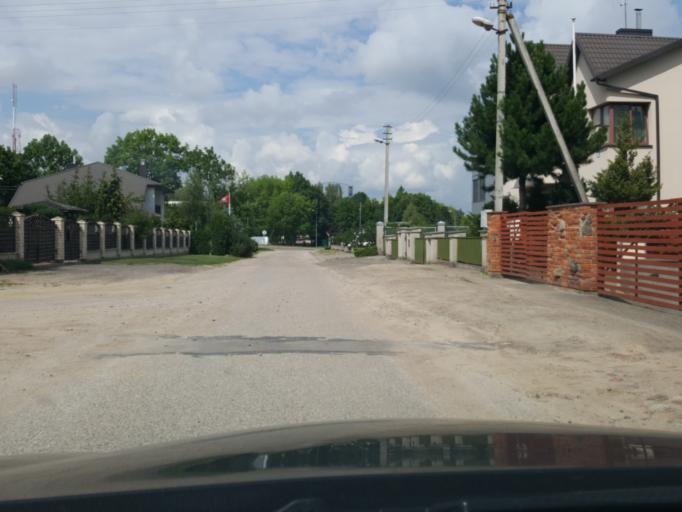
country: LT
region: Alytaus apskritis
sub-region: Alytus
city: Alytus
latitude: 54.3856
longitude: 24.0317
